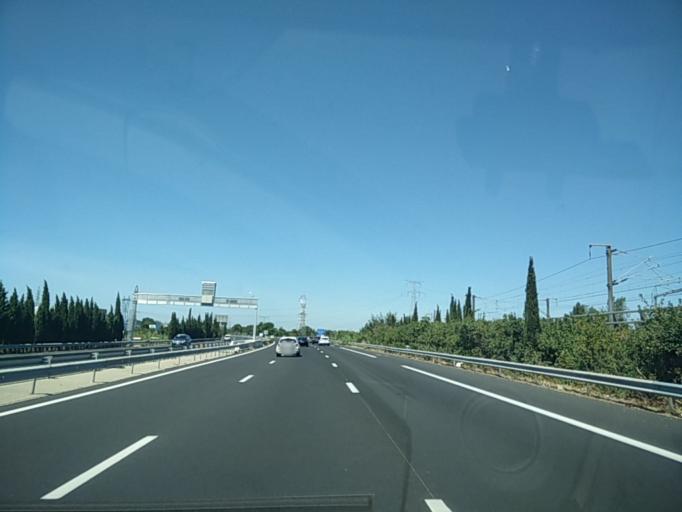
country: FR
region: Provence-Alpes-Cote d'Azur
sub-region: Departement du Vaucluse
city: Cavaillon
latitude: 43.8255
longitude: 5.0248
